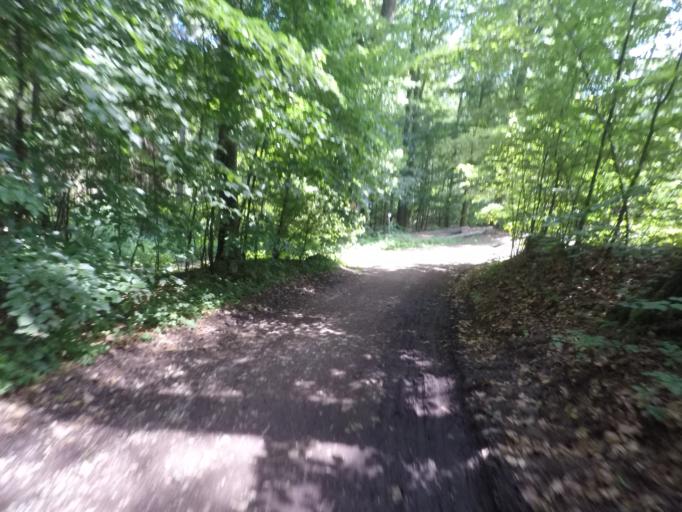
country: DE
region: North Rhine-Westphalia
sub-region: Regierungsbezirk Detmold
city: Bielefeld
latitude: 52.0145
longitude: 8.4825
